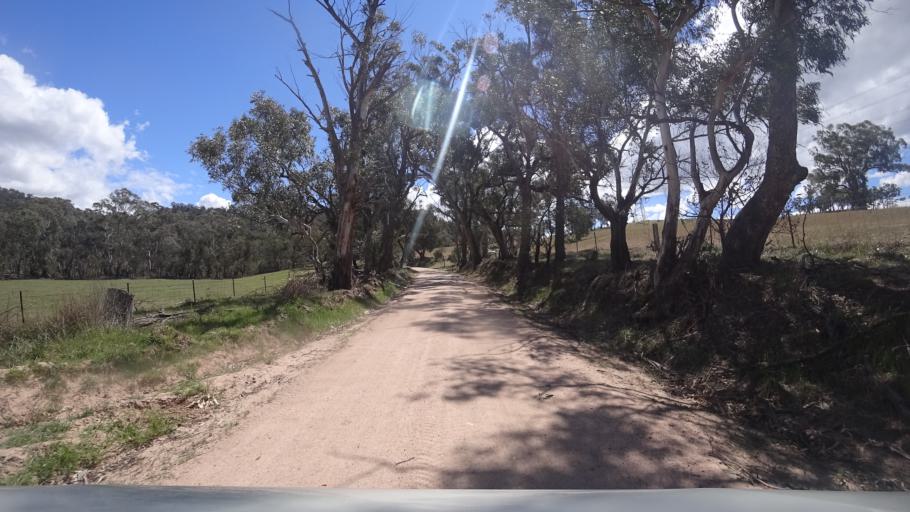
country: AU
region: New South Wales
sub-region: Oberon
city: Oberon
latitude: -33.5526
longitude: 149.9317
